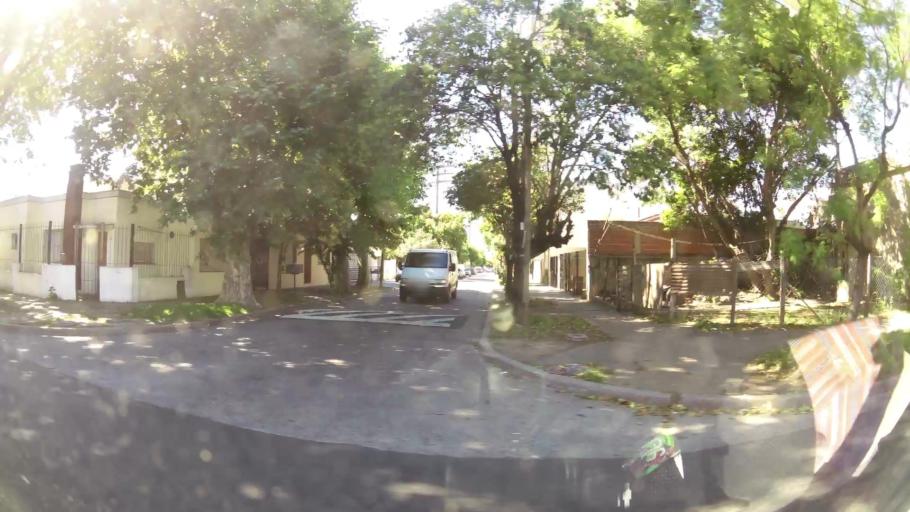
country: AR
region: Buenos Aires
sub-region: Partido de General San Martin
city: General San Martin
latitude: -34.5340
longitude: -58.5249
